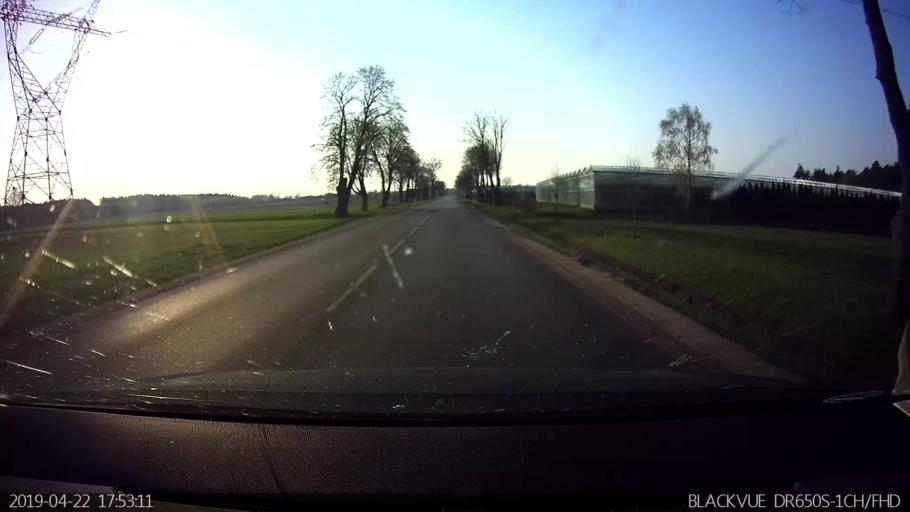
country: PL
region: Masovian Voivodeship
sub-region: Powiat wegrowski
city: Liw
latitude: 52.4507
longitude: 21.9595
